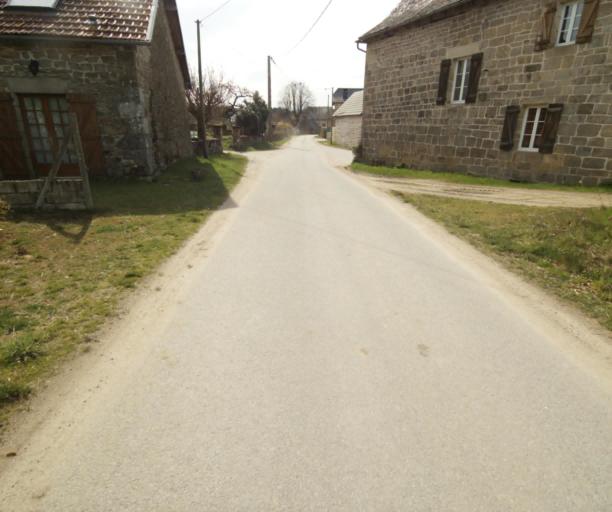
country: FR
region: Limousin
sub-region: Departement de la Correze
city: Correze
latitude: 45.3663
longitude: 1.8850
